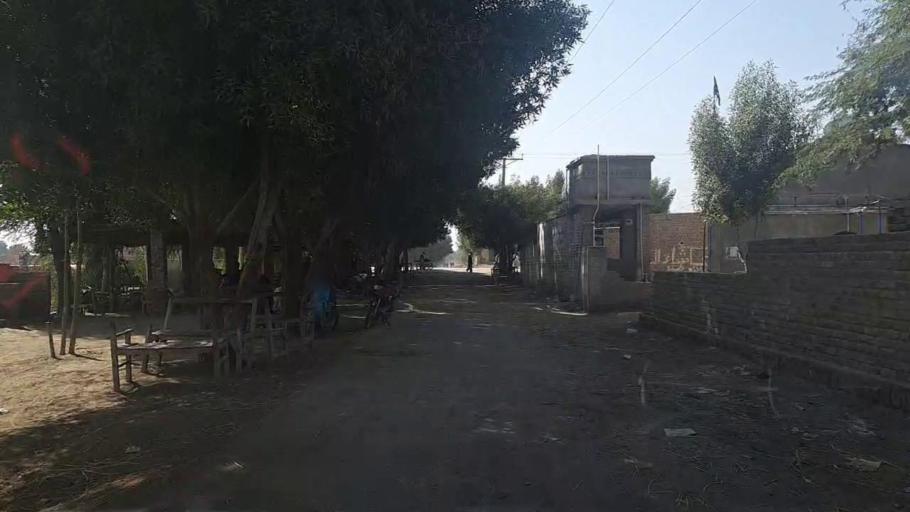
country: PK
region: Sindh
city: Thul
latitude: 28.2377
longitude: 68.7903
